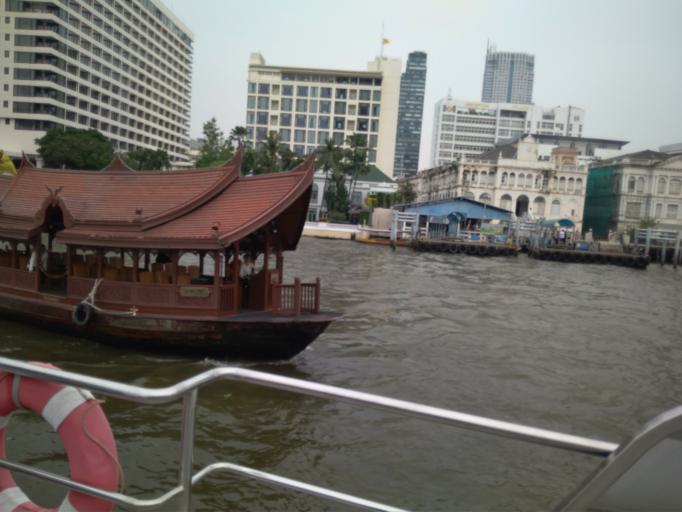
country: TH
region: Bangkok
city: Samphanthawong
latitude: 13.7233
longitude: 100.5130
